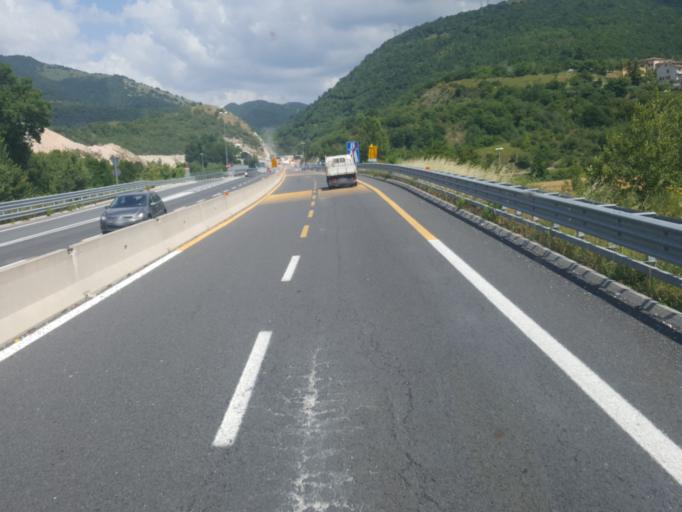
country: IT
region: Umbria
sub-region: Provincia di Perugia
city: Fossato di Vico
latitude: 43.3000
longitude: 12.7544
